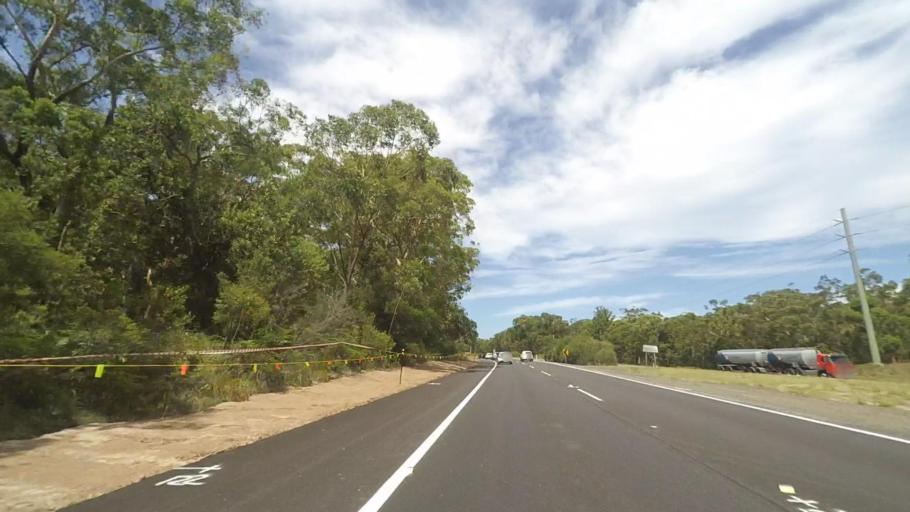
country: AU
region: New South Wales
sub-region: Port Stephens Shire
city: Anna Bay
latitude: -32.7791
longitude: 151.9998
